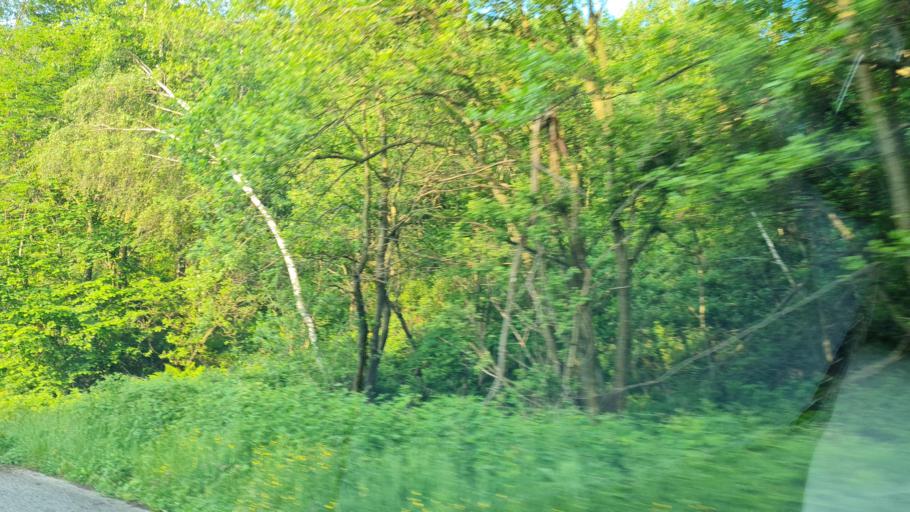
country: IT
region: Piedmont
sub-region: Provincia di Biella
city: Sordevolo
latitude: 45.5974
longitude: 7.9743
